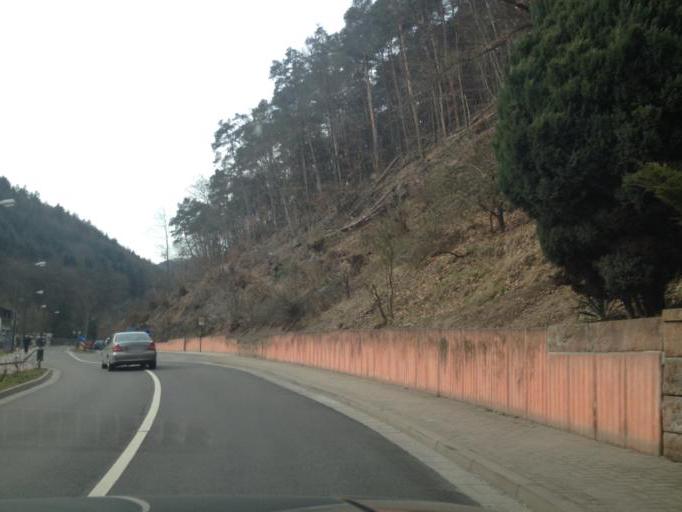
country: DE
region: Rheinland-Pfalz
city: Bad Duerkheim
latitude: 49.4634
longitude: 8.1232
